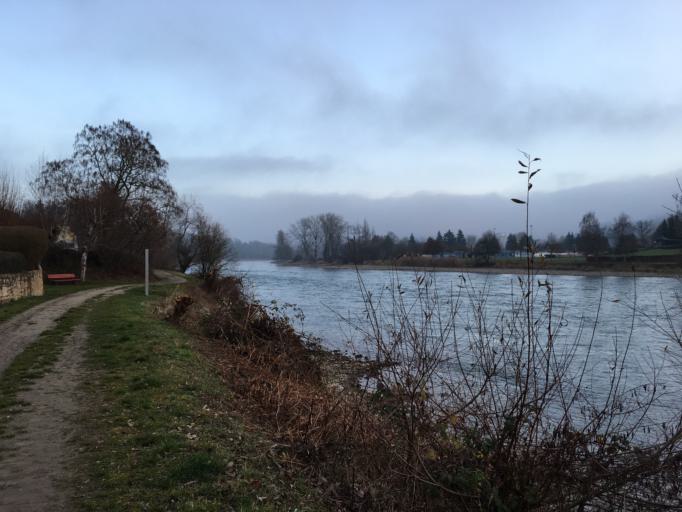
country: CH
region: Aargau
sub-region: Bezirk Zurzach
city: Bad Zurzach
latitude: 47.5861
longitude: 8.3042
